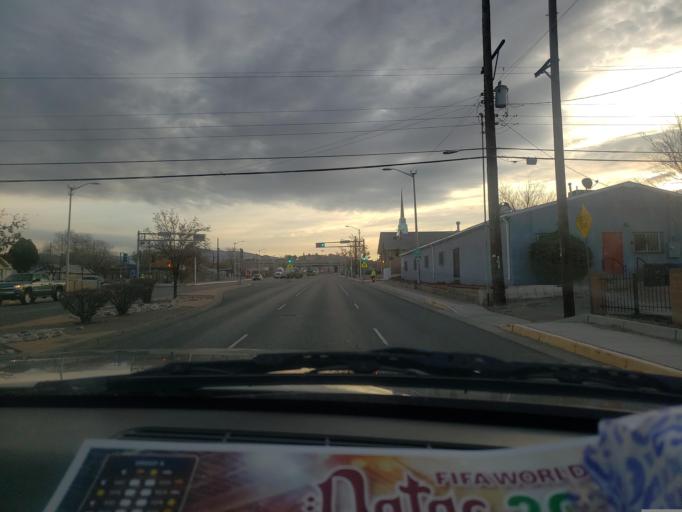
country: US
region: New Mexico
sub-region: Bernalillo County
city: Albuquerque
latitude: 35.0696
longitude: -106.6439
